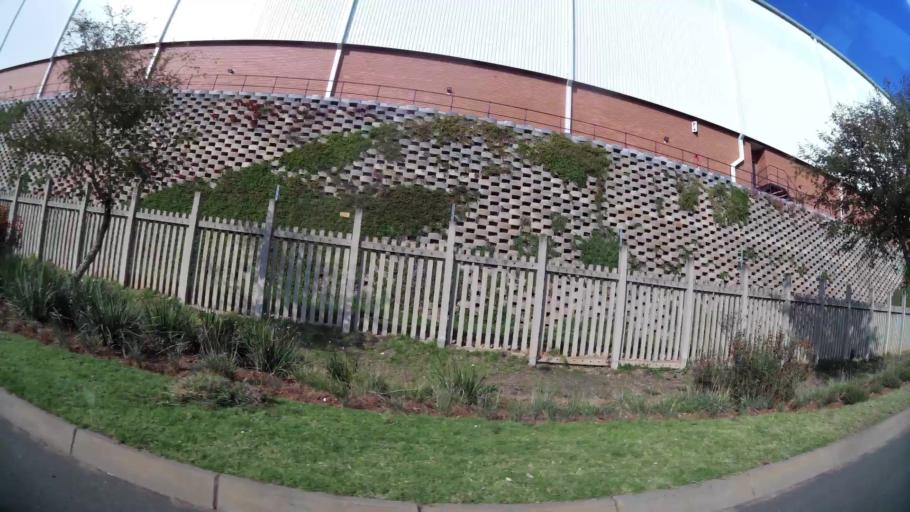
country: ZA
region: Gauteng
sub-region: City of Johannesburg Metropolitan Municipality
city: Modderfontein
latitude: -26.1045
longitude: 28.1432
